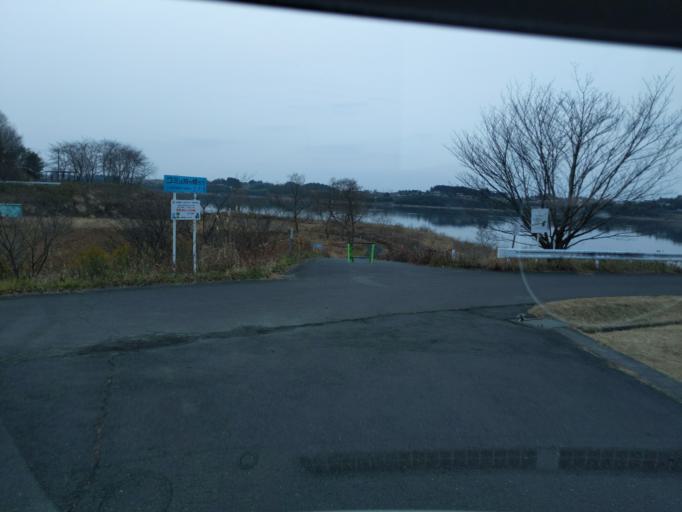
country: JP
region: Miyagi
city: Wakuya
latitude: 38.6987
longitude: 141.1456
